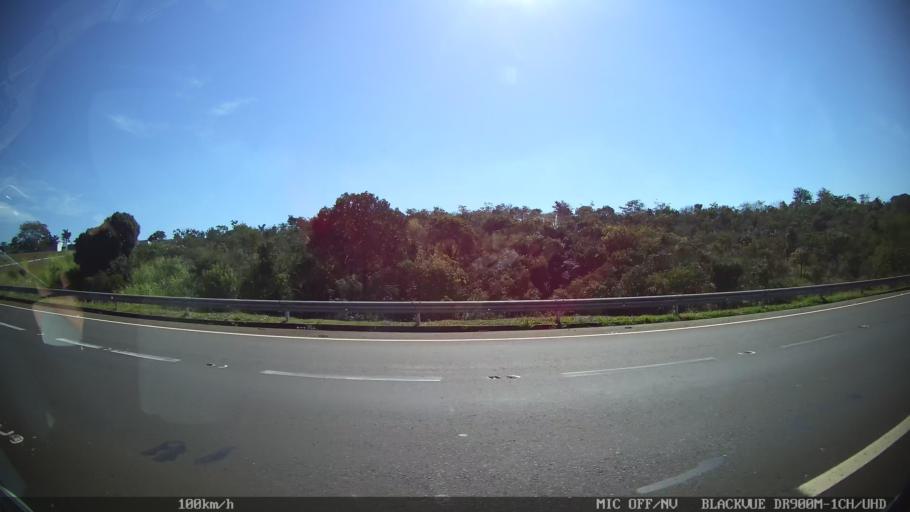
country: BR
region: Sao Paulo
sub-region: Franca
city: Franca
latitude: -20.5568
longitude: -47.4376
